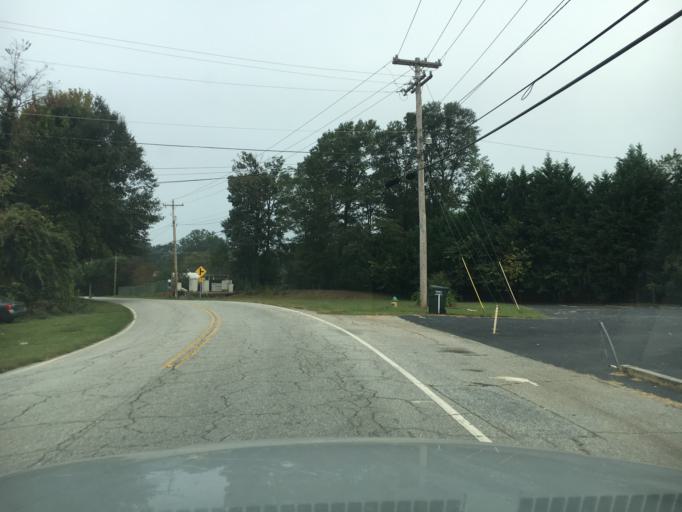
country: US
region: South Carolina
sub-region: Greenville County
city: Greer
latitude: 34.9442
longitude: -82.2567
